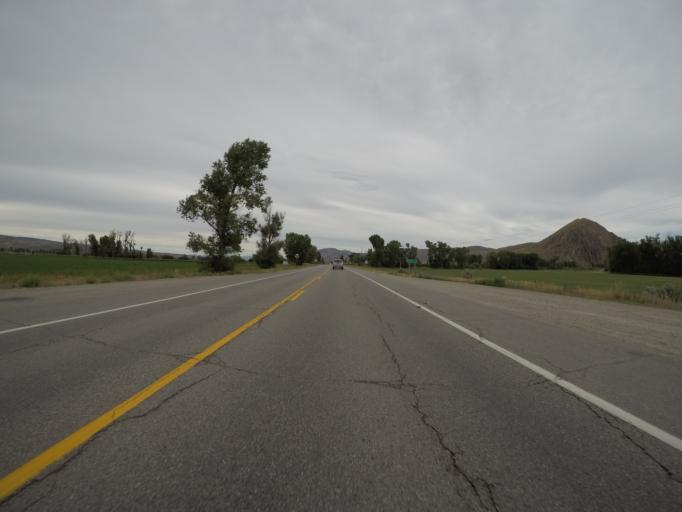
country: US
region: Idaho
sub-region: Bear Lake County
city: Montpelier
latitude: 42.0899
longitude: -110.9496
